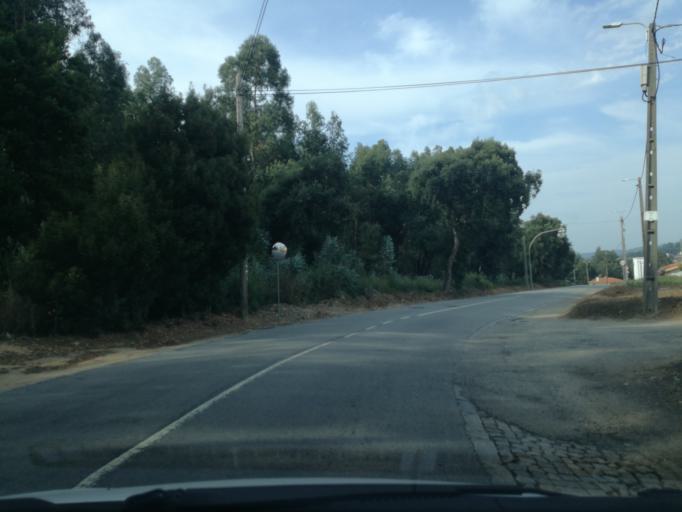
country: PT
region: Porto
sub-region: Vila Nova de Gaia
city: Sao Felix da Marinha
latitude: 41.0272
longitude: -8.6303
